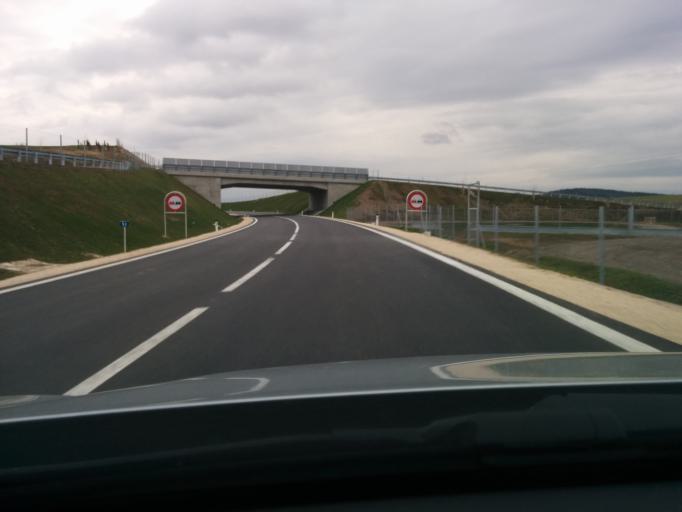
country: AT
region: Lower Austria
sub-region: Politischer Bezirk Mistelbach
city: Mistelbach
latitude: 48.5715
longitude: 16.5545
